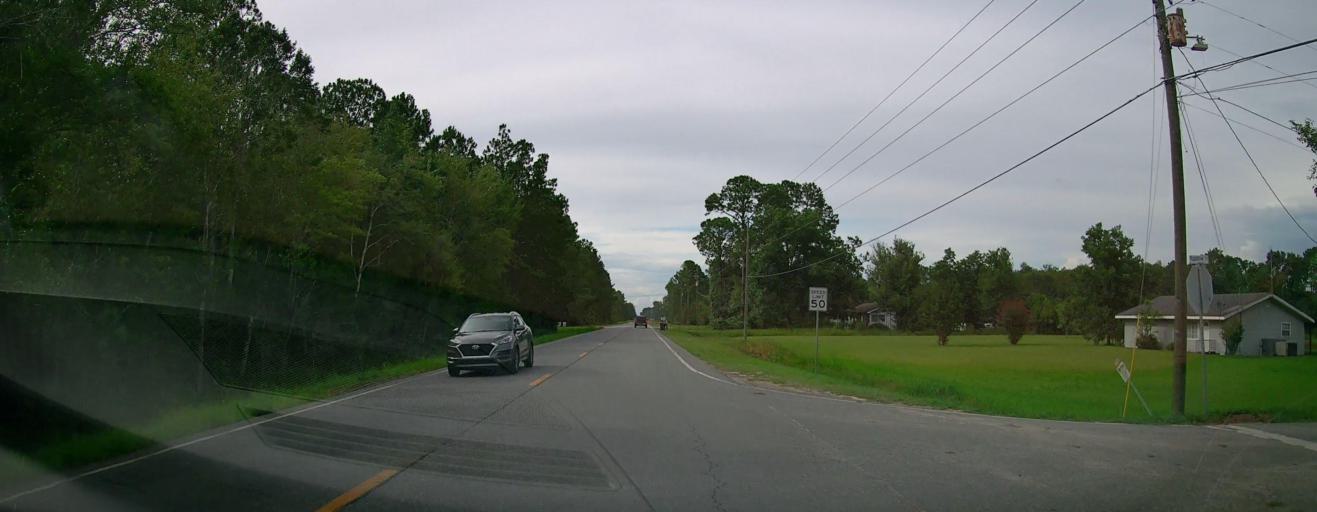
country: US
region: Georgia
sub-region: Wayne County
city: Jesup
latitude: 31.6358
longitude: -81.9034
